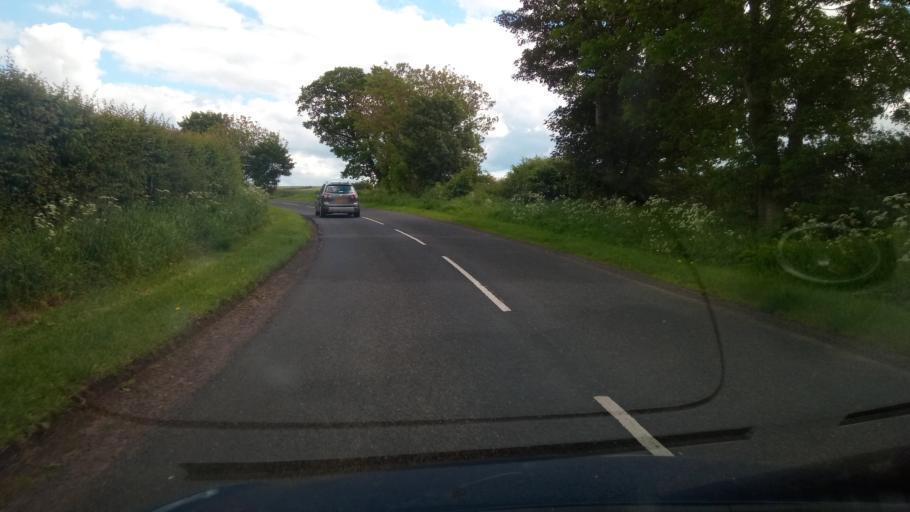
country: GB
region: Scotland
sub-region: The Scottish Borders
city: Coldstream
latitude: 55.6032
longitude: -2.2846
